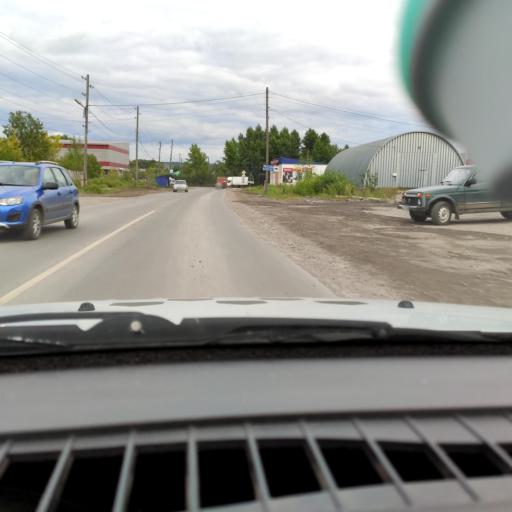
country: RU
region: Perm
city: Chusovoy
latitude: 58.3001
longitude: 57.8130
